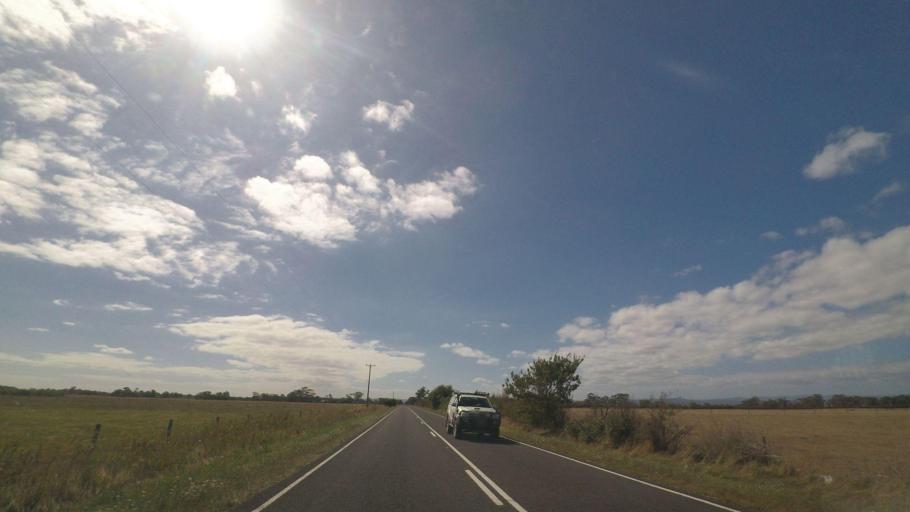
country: AU
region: Victoria
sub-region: Cardinia
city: Garfield
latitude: -38.2022
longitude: 145.6301
